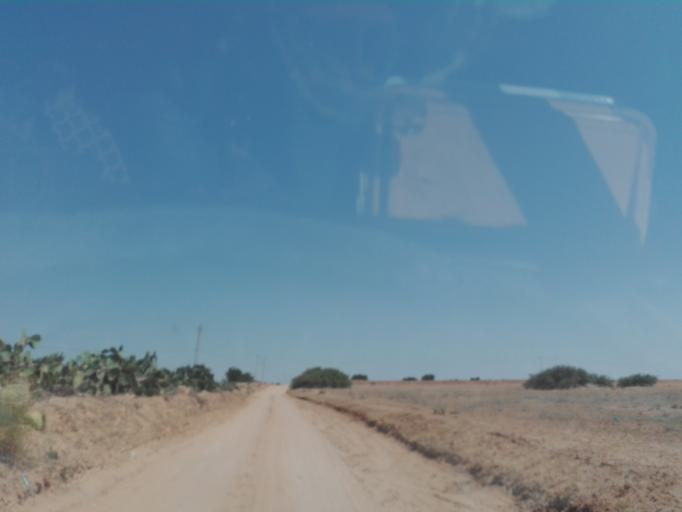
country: TN
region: Safaqis
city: Bi'r `Ali Bin Khalifah
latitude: 34.6717
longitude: 10.2347
